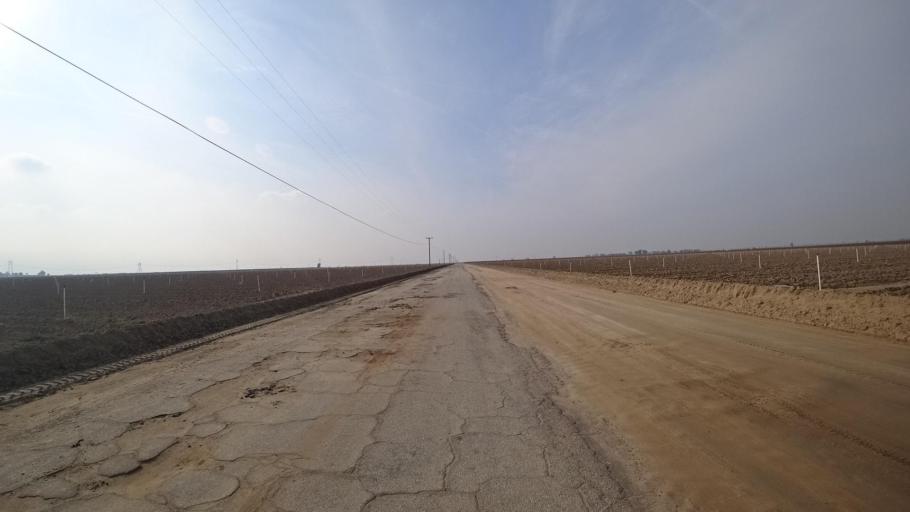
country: US
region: California
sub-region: Kern County
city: Weedpatch
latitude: 35.1359
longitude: -118.9785
